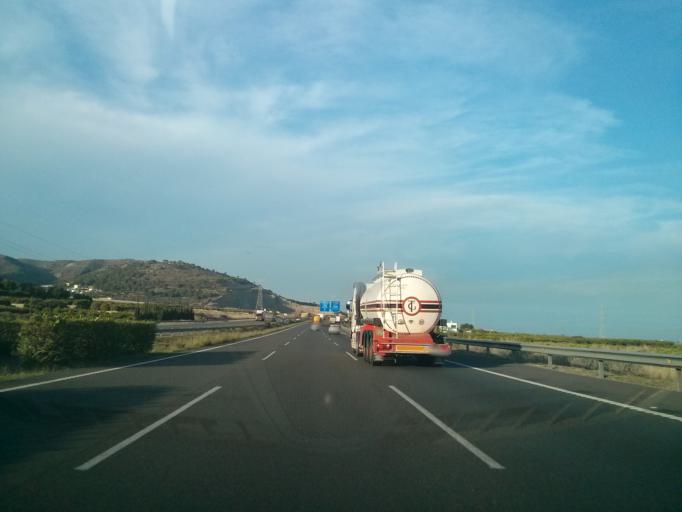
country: ES
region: Valencia
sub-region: Provincia de Valencia
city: Petres
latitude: 39.6912
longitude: -0.2848
